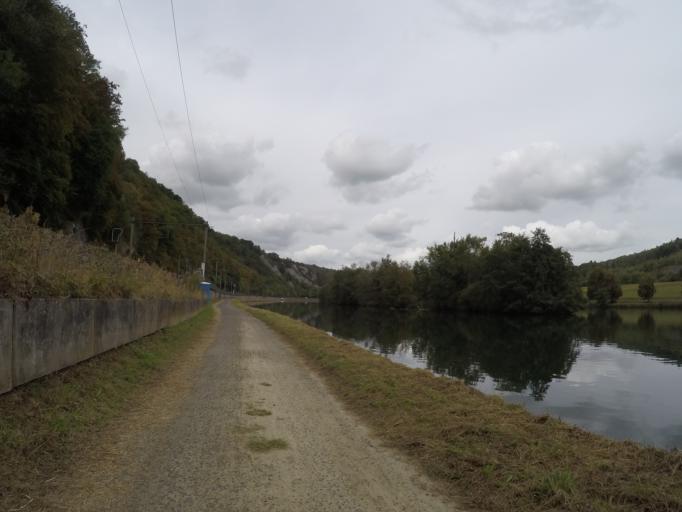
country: BE
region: Wallonia
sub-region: Province de Namur
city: Dinant
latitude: 50.2811
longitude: 4.8926
